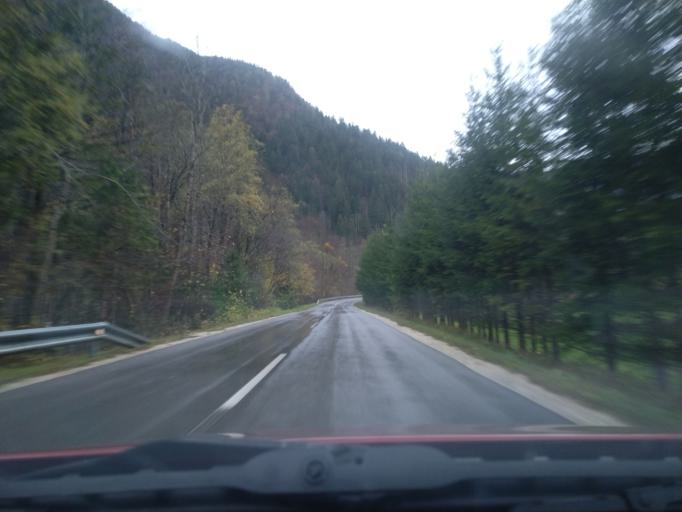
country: SI
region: Solcava
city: Solcava
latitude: 46.4055
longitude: 14.7027
